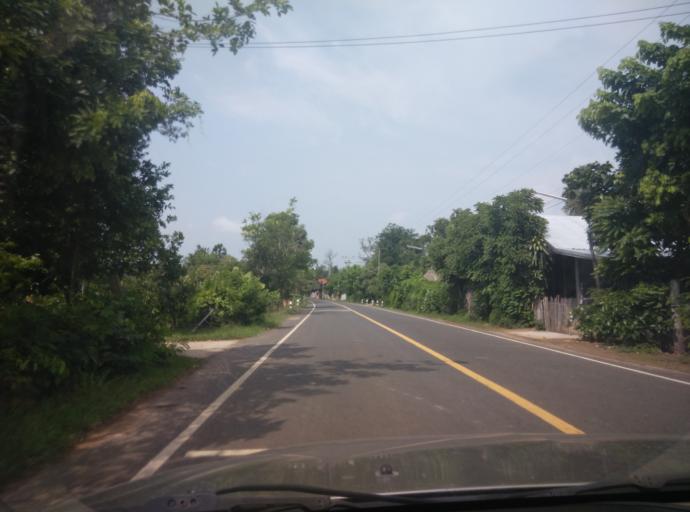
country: TH
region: Sisaket
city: Huai Thap Than
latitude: 15.0316
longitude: 104.0754
